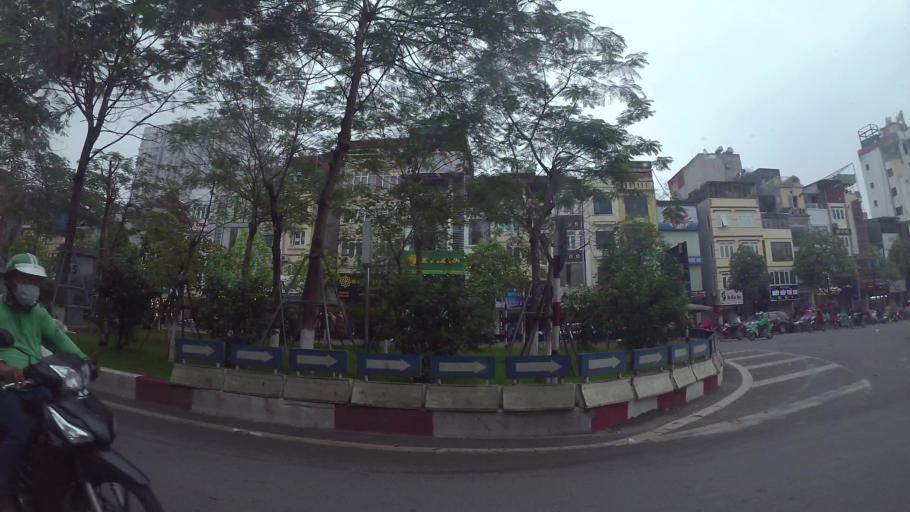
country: VN
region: Ha Noi
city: Dong Da
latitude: 21.0192
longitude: 105.8284
